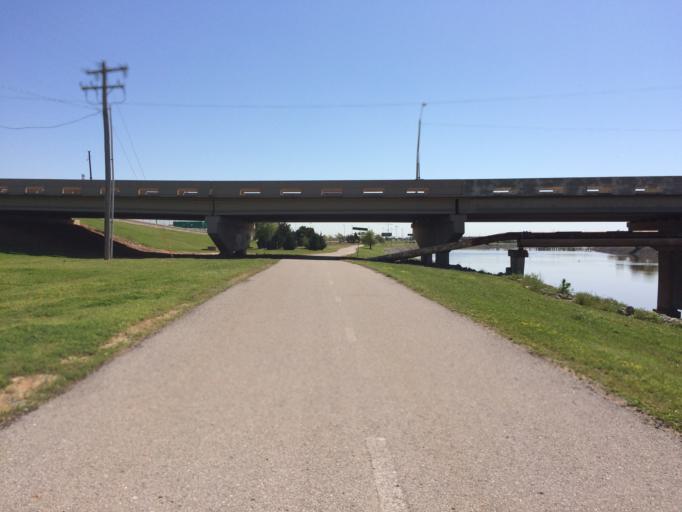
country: US
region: Oklahoma
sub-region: Oklahoma County
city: Oklahoma City
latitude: 35.4607
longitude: -97.5485
